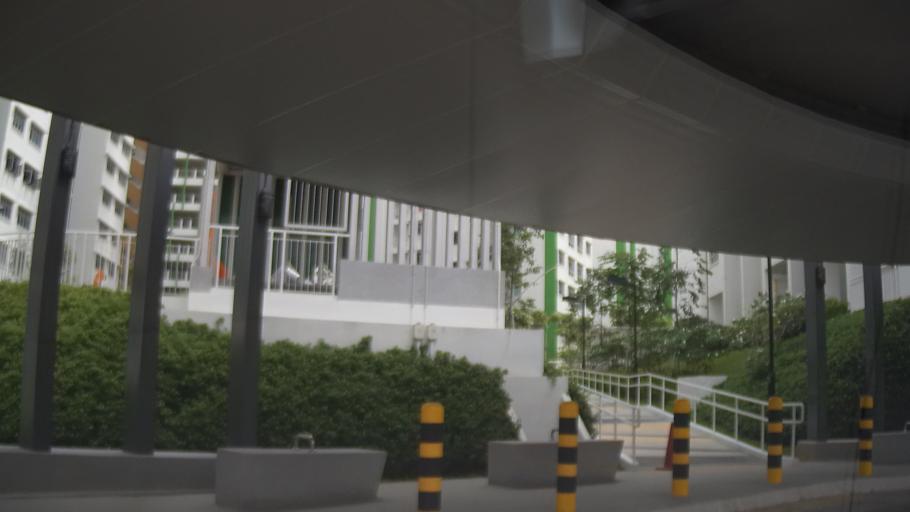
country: MY
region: Johor
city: Johor Bahru
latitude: 1.4360
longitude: 103.7754
